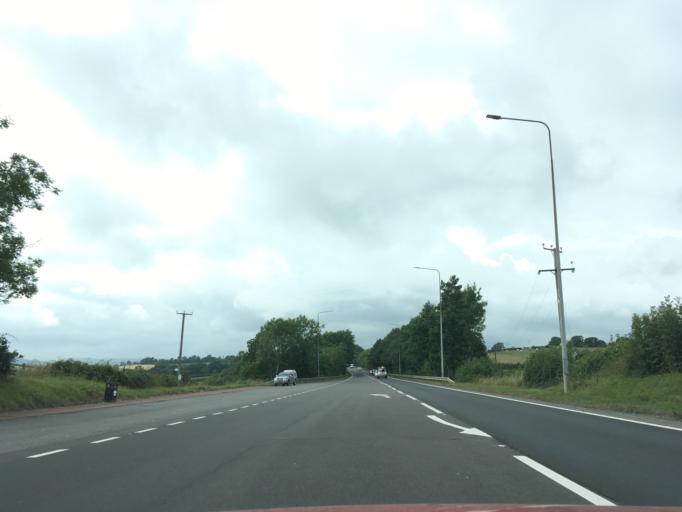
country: GB
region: Wales
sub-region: Carmarthenshire
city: Saint Clears
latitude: 51.8200
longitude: -4.5156
